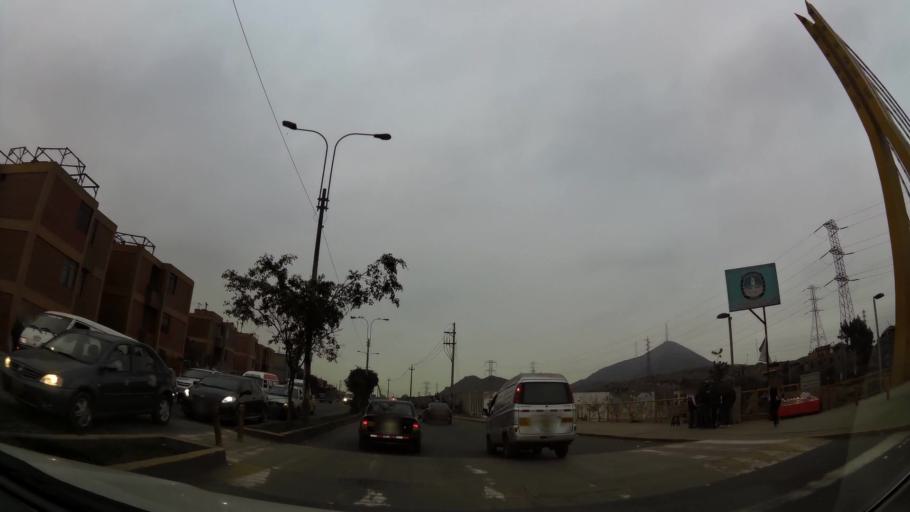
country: PE
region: Lima
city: Lima
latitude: -12.0264
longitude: -76.9885
